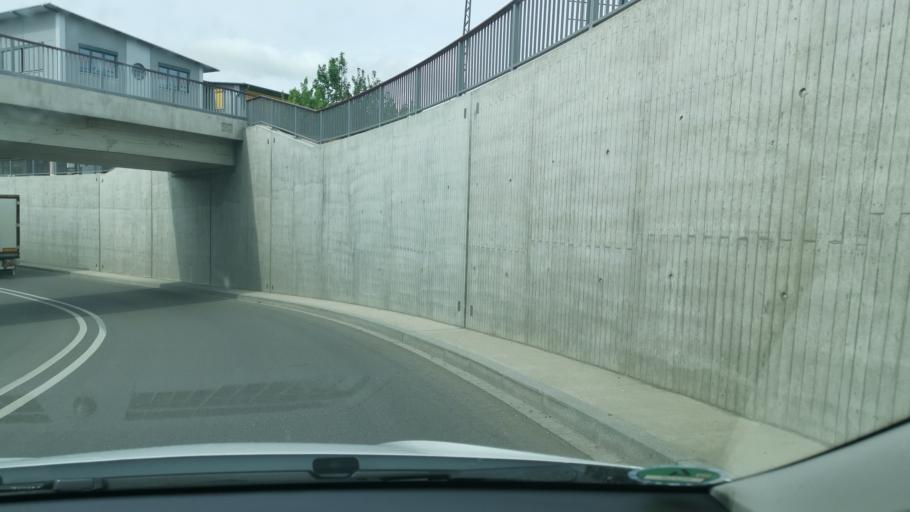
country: DE
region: Bavaria
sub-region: Swabia
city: Aichach
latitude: 48.4642
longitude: 11.1250
